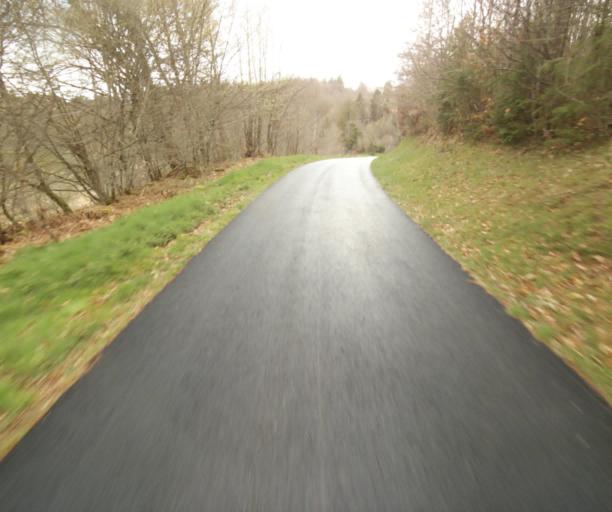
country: FR
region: Limousin
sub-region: Departement de la Correze
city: Saint-Privat
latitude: 45.2151
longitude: 2.0157
